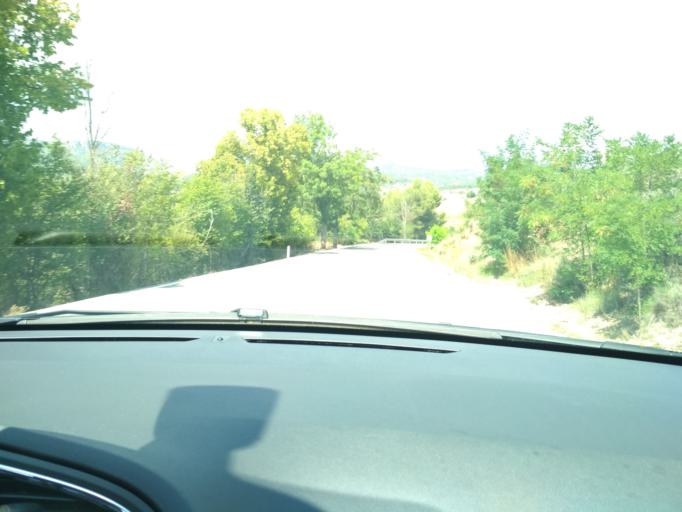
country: ES
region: Aragon
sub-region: Provincia de Teruel
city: Rubielos de Mora
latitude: 40.1912
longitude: -0.6455
